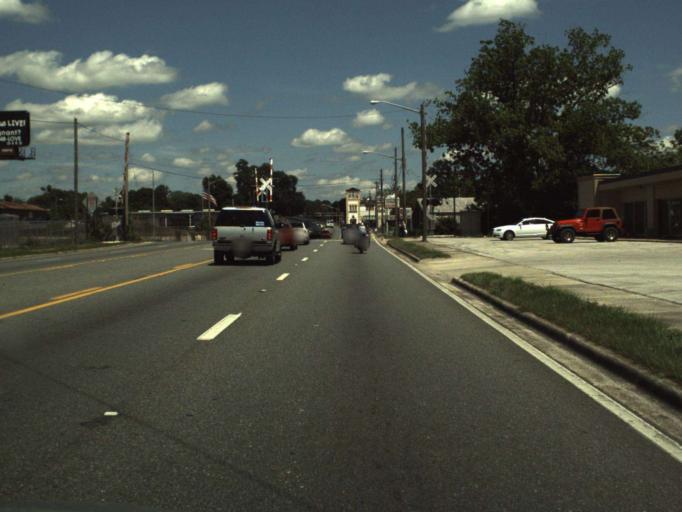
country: US
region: Florida
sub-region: Marion County
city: Ocala
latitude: 29.1969
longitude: -82.1399
